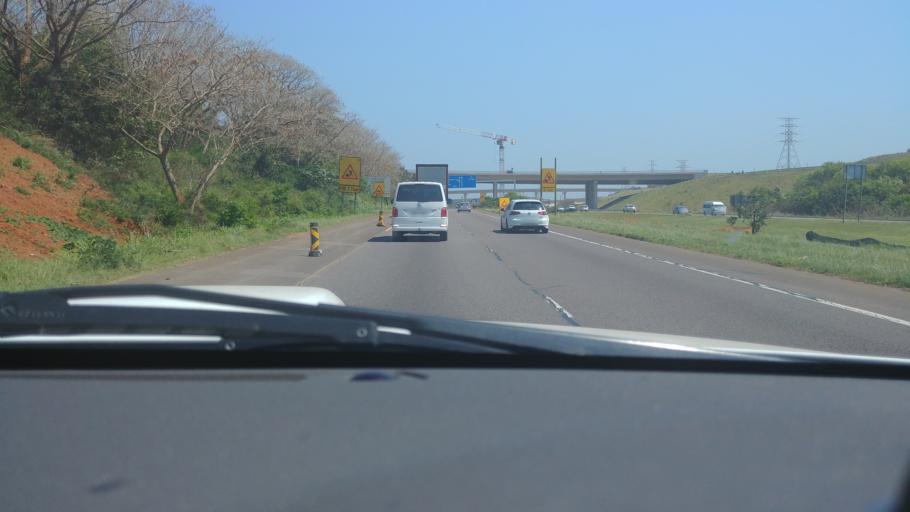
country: ZA
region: KwaZulu-Natal
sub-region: eThekwini Metropolitan Municipality
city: Durban
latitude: -29.7123
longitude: 31.0655
